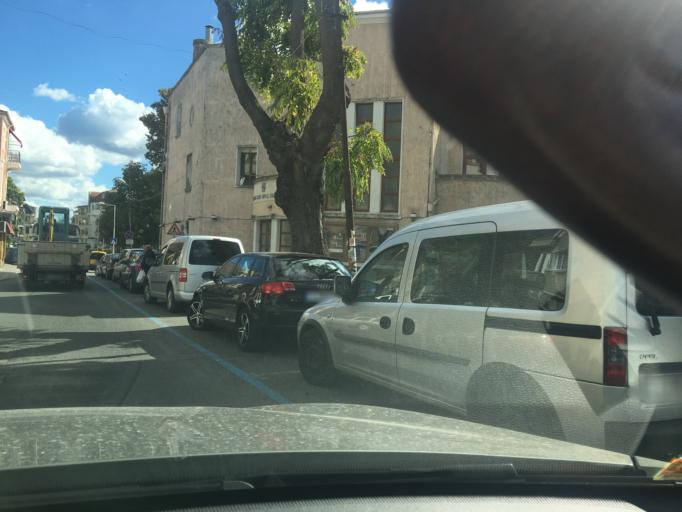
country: BG
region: Burgas
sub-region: Obshtina Burgas
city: Burgas
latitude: 42.4971
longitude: 27.4734
